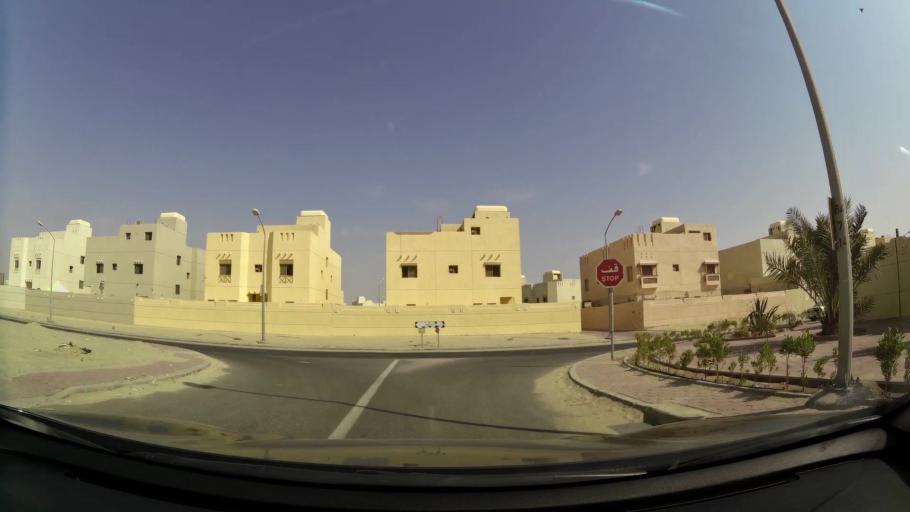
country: KW
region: Al Ahmadi
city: Al Wafrah
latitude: 28.8074
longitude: 48.0594
